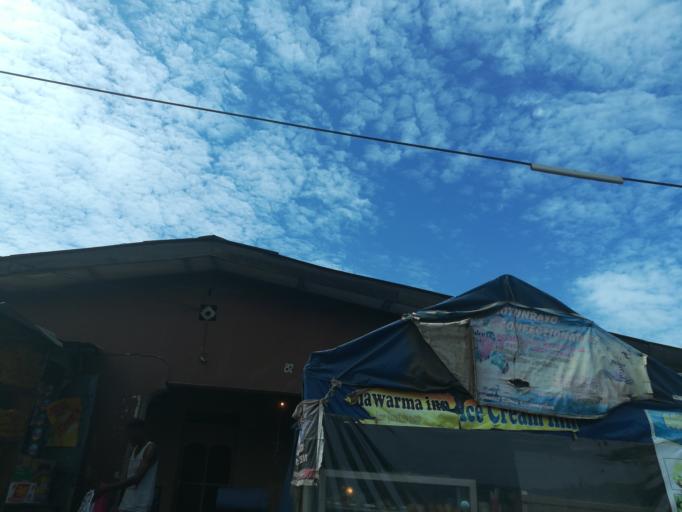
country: NG
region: Lagos
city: Oshodi
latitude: 6.5550
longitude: 3.3316
